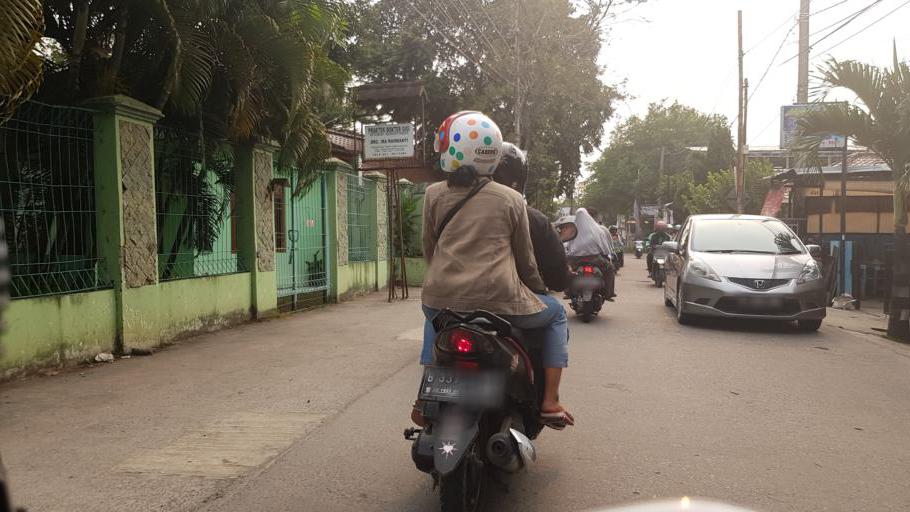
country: ID
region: West Java
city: Depok
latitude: -6.3725
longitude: 106.8458
